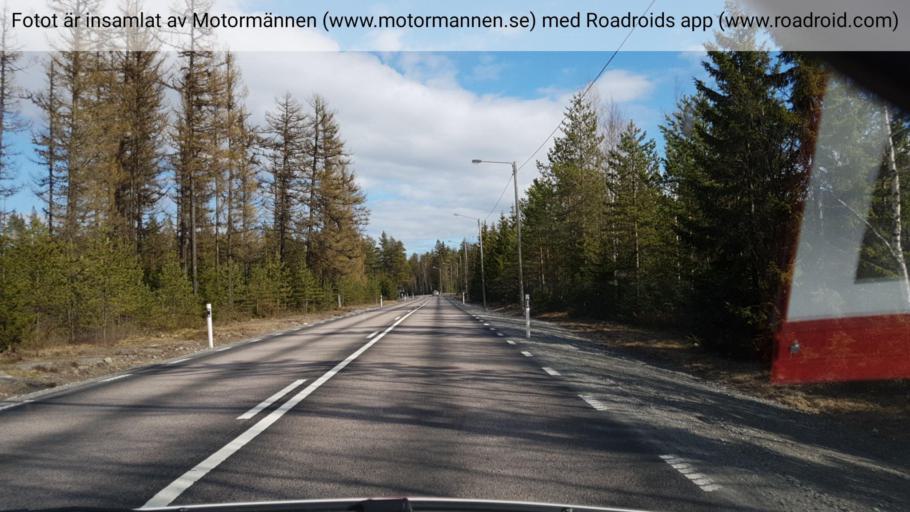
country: SE
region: Vaesternorrland
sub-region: Solleftea Kommun
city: Solleftea
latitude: 63.1504
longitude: 17.3384
